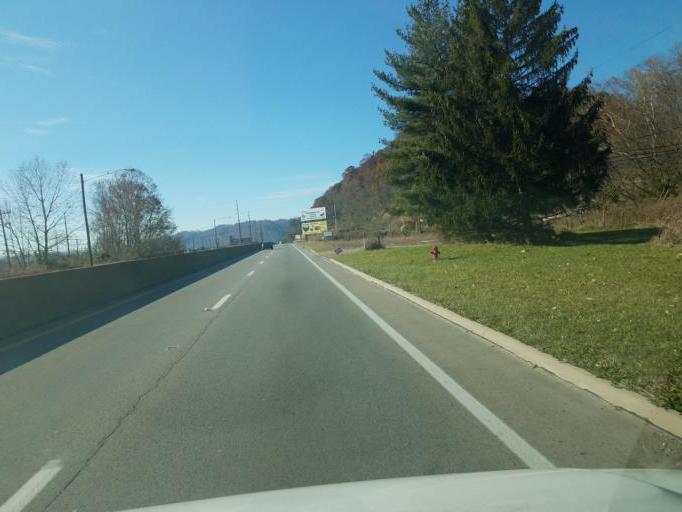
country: US
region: Ohio
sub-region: Scioto County
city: New Boston
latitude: 38.7555
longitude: -82.9093
